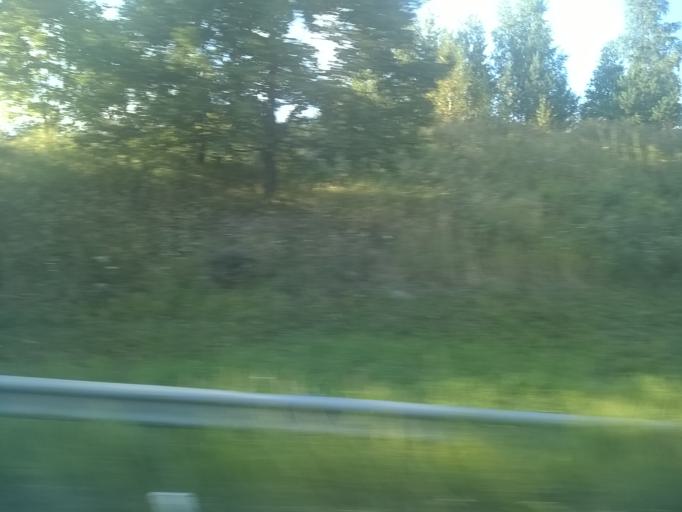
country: FI
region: Pirkanmaa
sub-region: Tampere
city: Tampere
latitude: 61.4629
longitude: 23.7697
